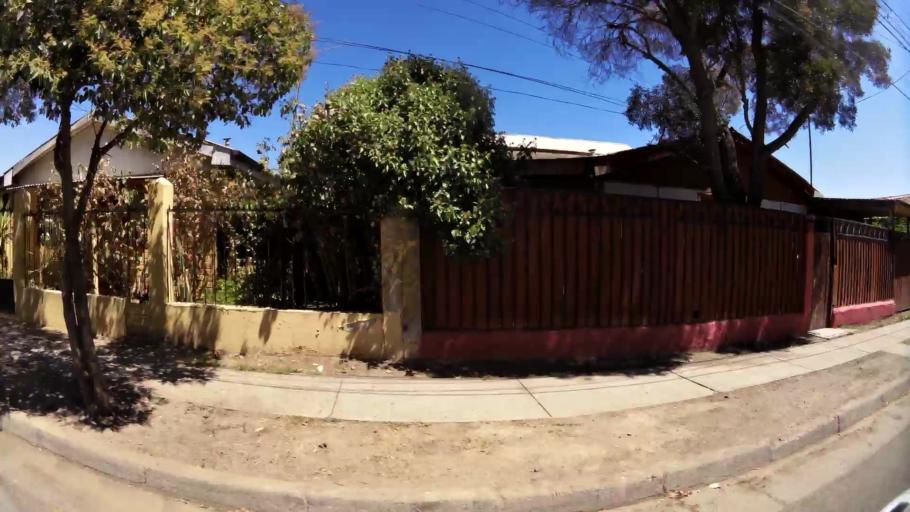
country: CL
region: O'Higgins
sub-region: Provincia de Cachapoal
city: Rancagua
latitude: -34.1605
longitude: -70.7538
